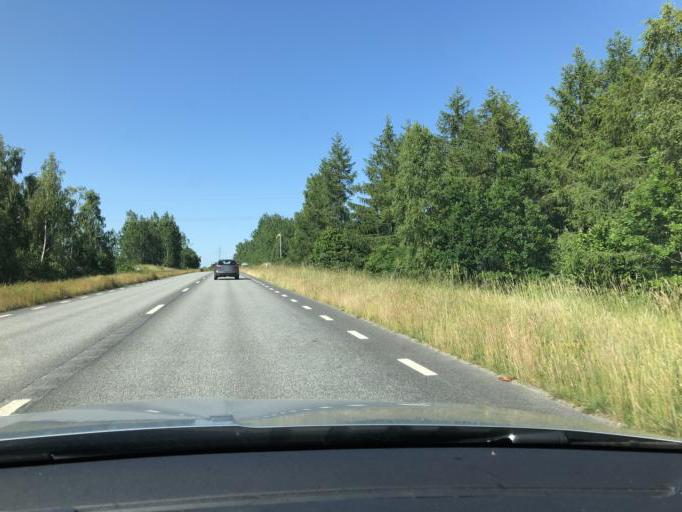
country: SE
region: Skane
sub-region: Bromolla Kommun
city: Bromoella
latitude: 56.0718
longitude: 14.4988
